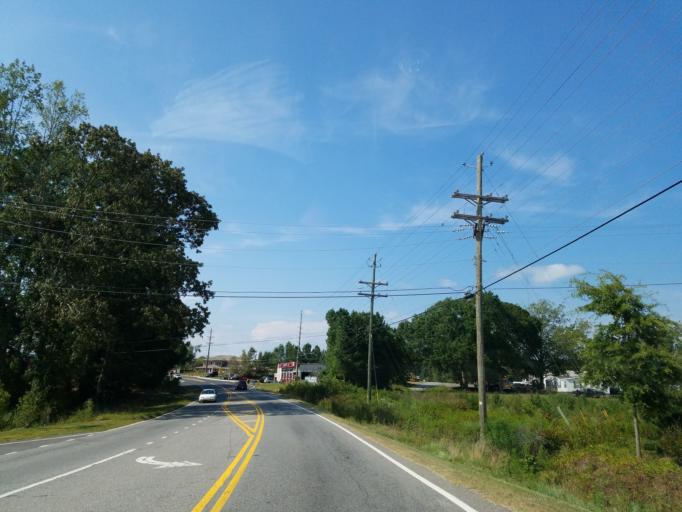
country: US
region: Georgia
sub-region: Dawson County
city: Dawsonville
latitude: 34.3586
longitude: -84.0322
